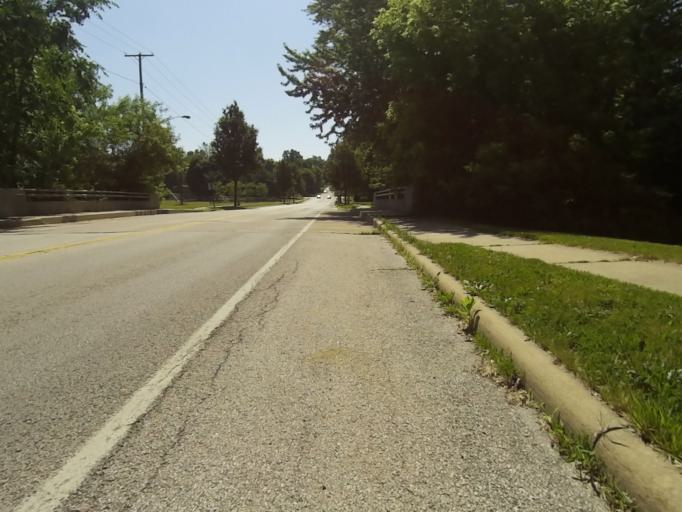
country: US
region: Ohio
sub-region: Portage County
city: Kent
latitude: 41.1619
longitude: -81.3700
